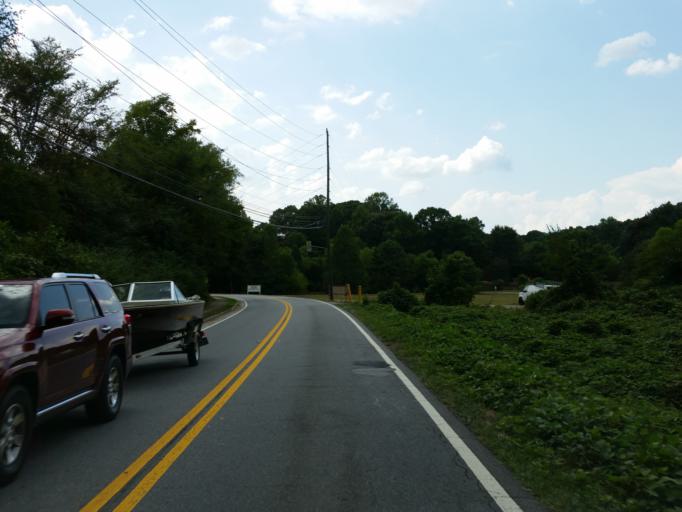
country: US
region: Georgia
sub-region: Cherokee County
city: Woodstock
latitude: 34.0498
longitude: -84.5025
